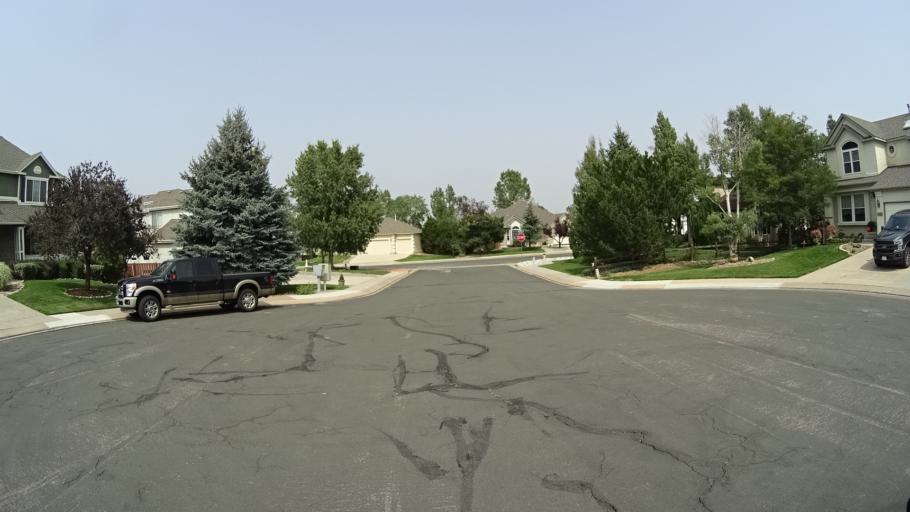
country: US
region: Colorado
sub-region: El Paso County
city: Cimarron Hills
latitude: 38.9154
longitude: -104.7471
